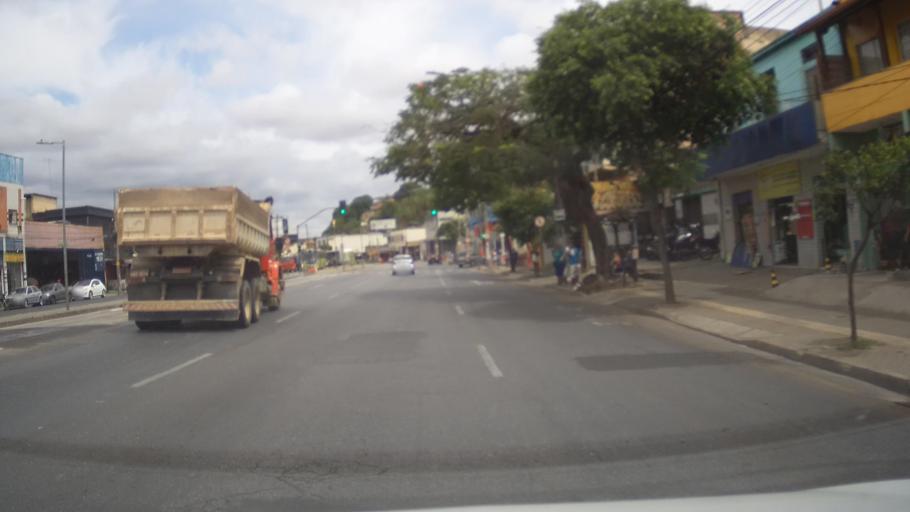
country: BR
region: Minas Gerais
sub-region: Belo Horizonte
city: Belo Horizonte
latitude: -19.8130
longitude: -43.9579
